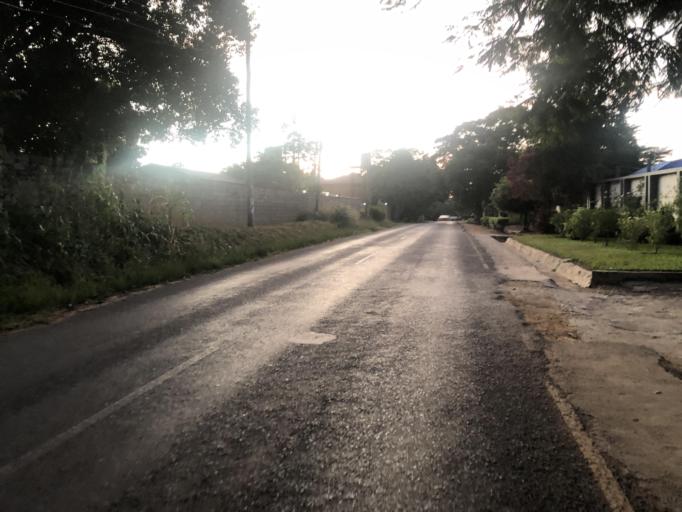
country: ZM
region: Lusaka
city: Lusaka
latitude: -15.3894
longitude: 28.3394
